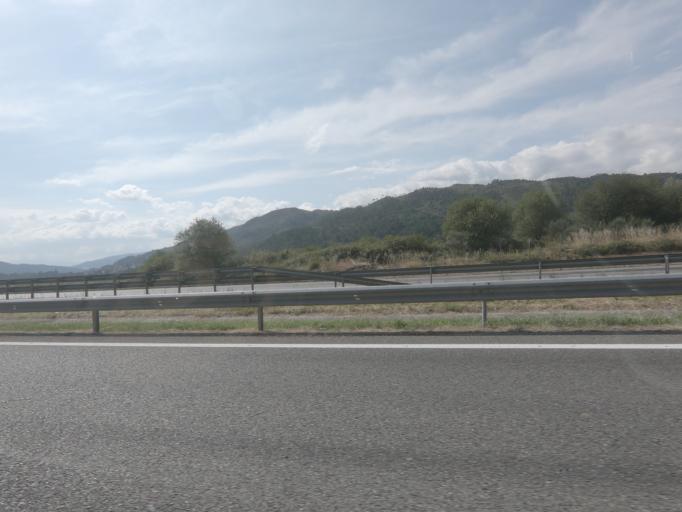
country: ES
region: Galicia
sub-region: Provincia de Ourense
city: Toen
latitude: 42.3404
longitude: -7.9295
